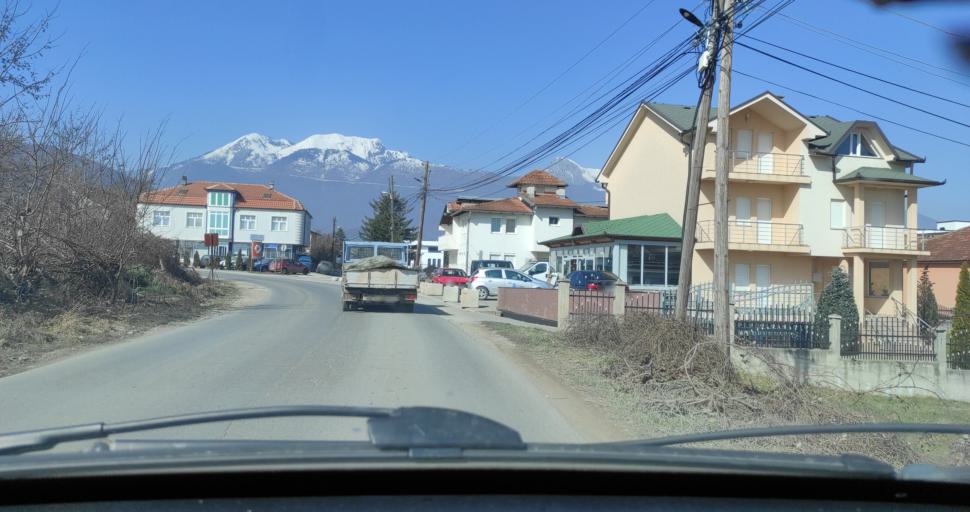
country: XK
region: Pec
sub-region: Komuna e Pejes
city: Peje
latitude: 42.6416
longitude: 20.3005
